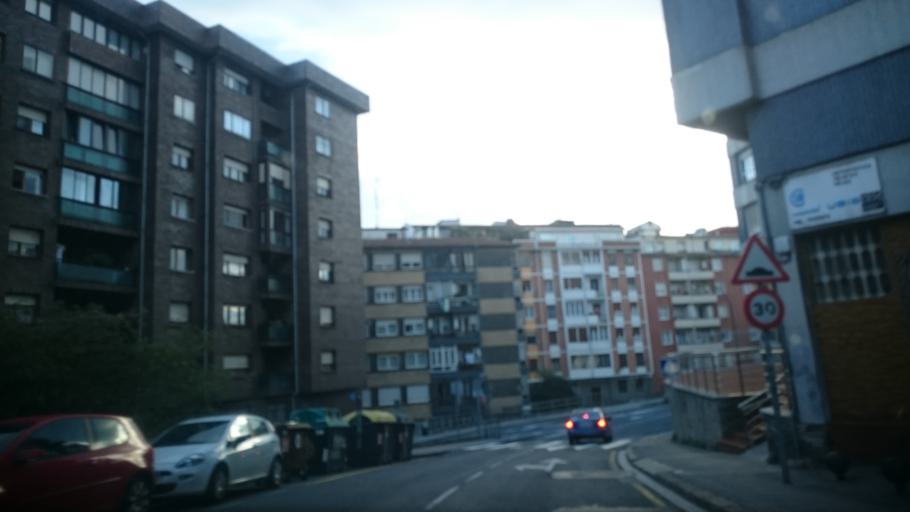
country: ES
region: Basque Country
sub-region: Bizkaia
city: Santutxu
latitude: 43.2575
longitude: -2.9152
